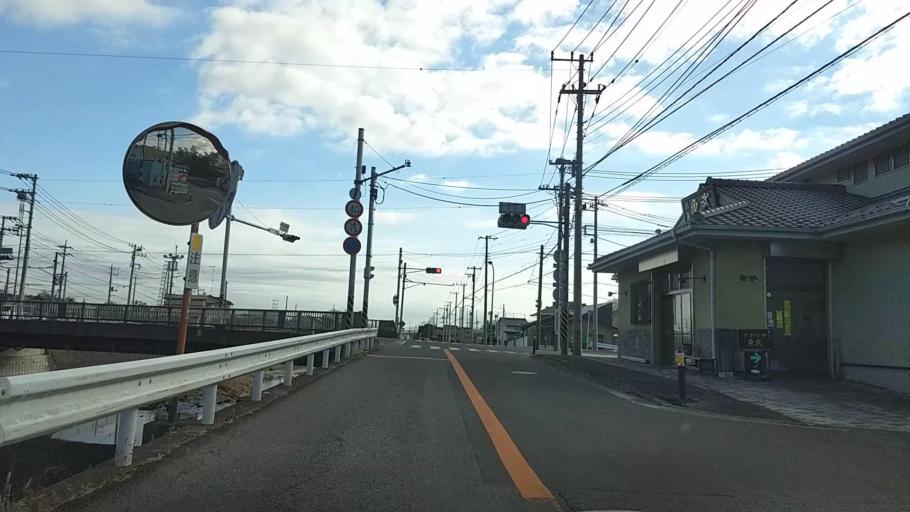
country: JP
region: Kanagawa
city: Atsugi
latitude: 35.4344
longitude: 139.3156
